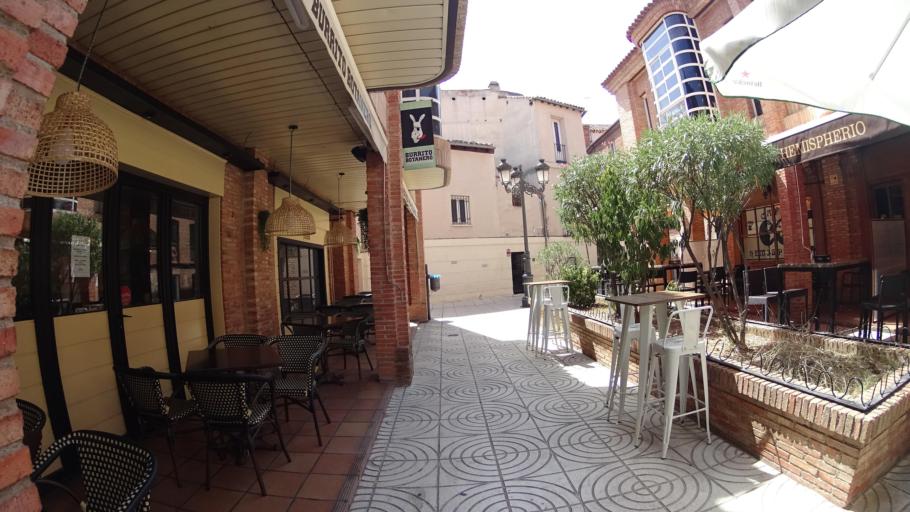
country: ES
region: Madrid
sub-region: Provincia de Madrid
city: Alcala de Henares
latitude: 40.4835
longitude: -3.3654
